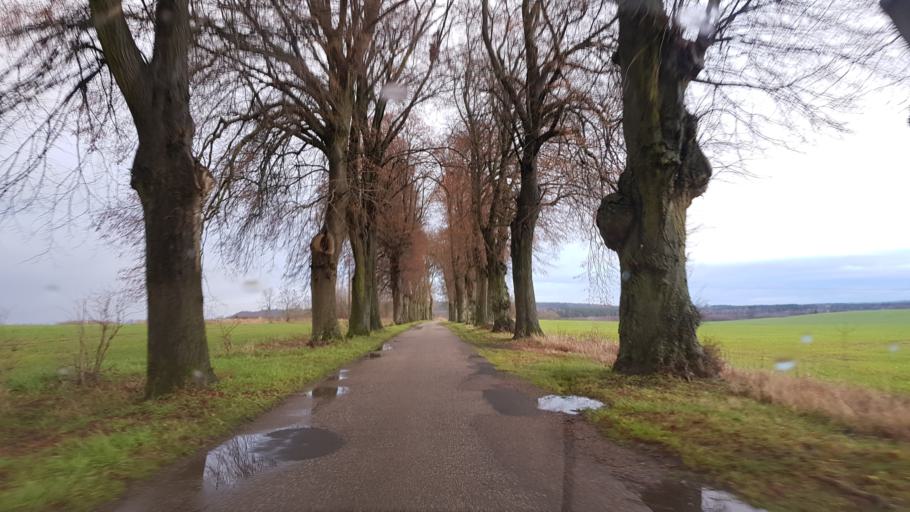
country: PL
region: West Pomeranian Voivodeship
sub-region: Powiat swidwinski
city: Rabino
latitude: 53.9440
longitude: 15.9250
